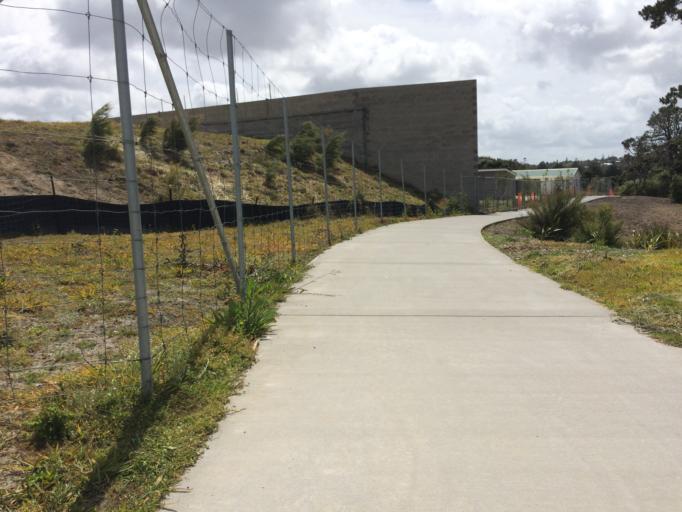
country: NZ
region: Auckland
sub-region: Auckland
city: Rosebank
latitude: -36.7957
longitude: 174.6690
